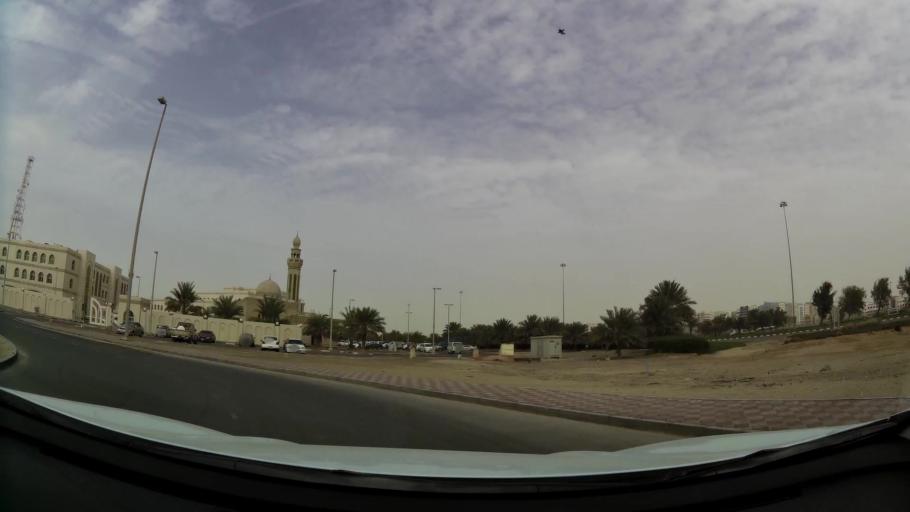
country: AE
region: Abu Dhabi
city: Abu Dhabi
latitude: 24.3376
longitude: 54.5255
